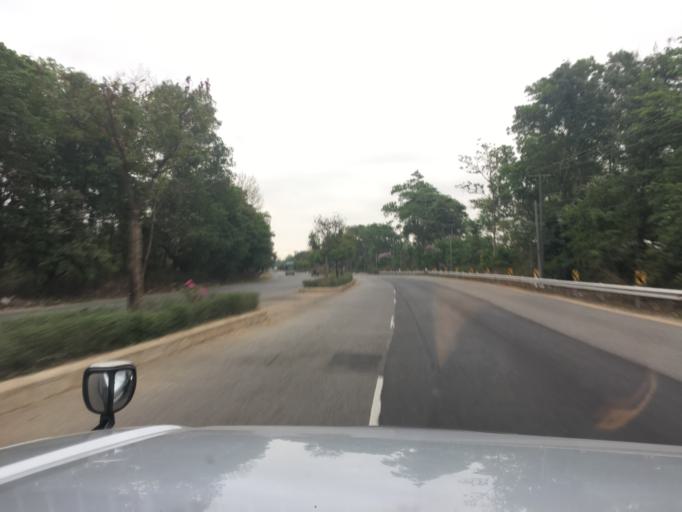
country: MM
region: Bago
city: Bago
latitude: 17.2225
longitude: 96.4433
